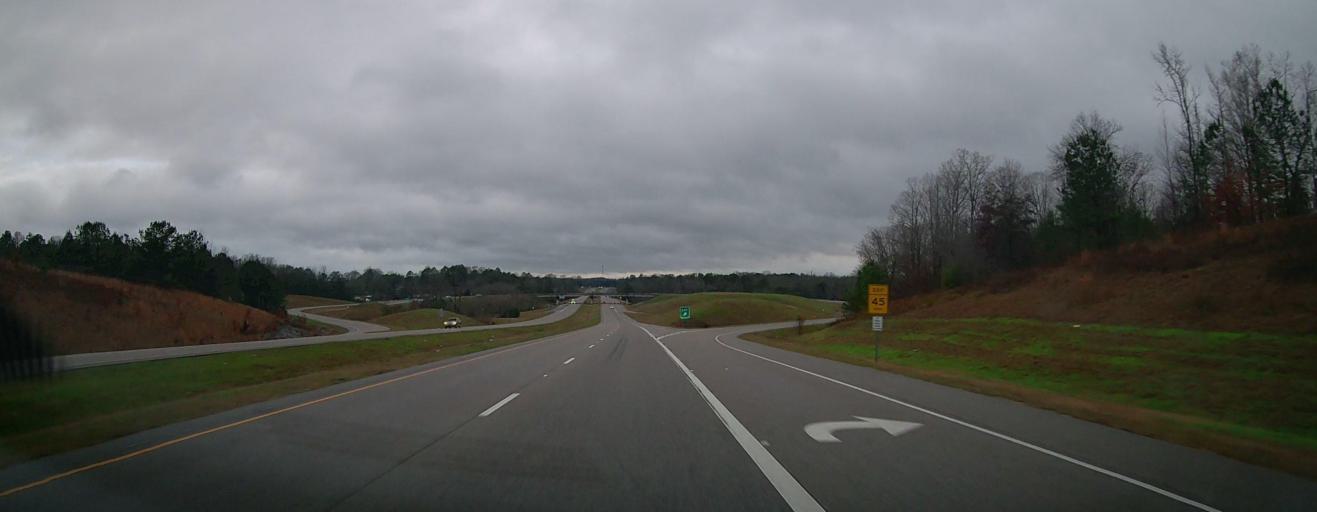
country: US
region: Alabama
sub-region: Bibb County
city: Centreville
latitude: 32.9571
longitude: -87.1292
